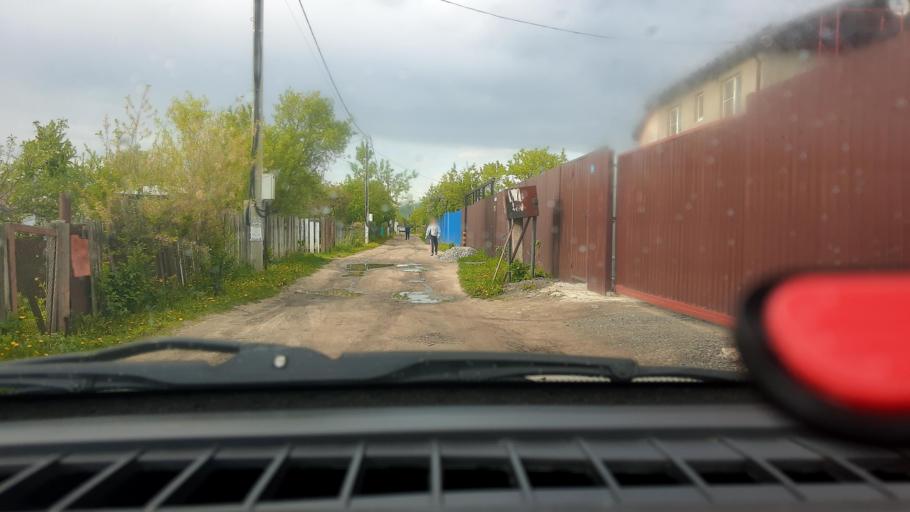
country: RU
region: Nizjnij Novgorod
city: Nizhniy Novgorod
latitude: 56.2671
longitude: 43.9541
